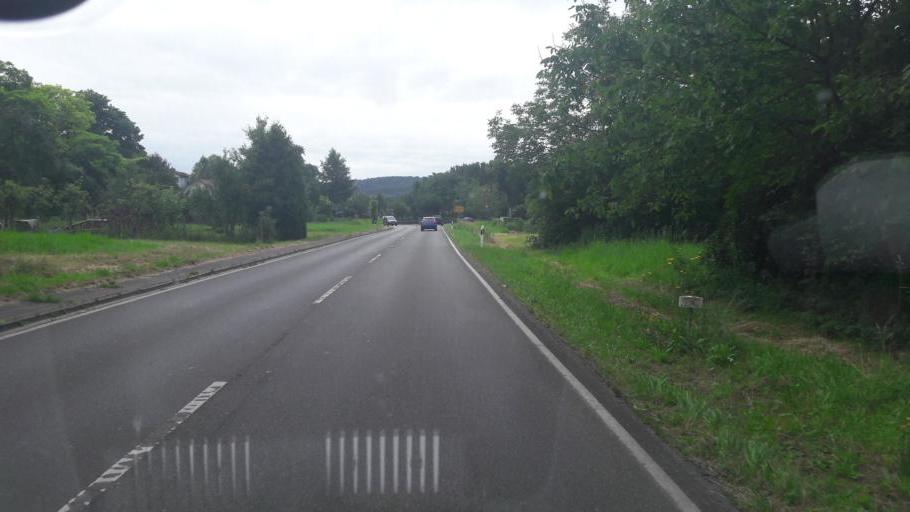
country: DE
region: Baden-Wuerttemberg
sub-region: Karlsruhe Region
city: Dielheim
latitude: 49.2904
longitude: 8.7307
